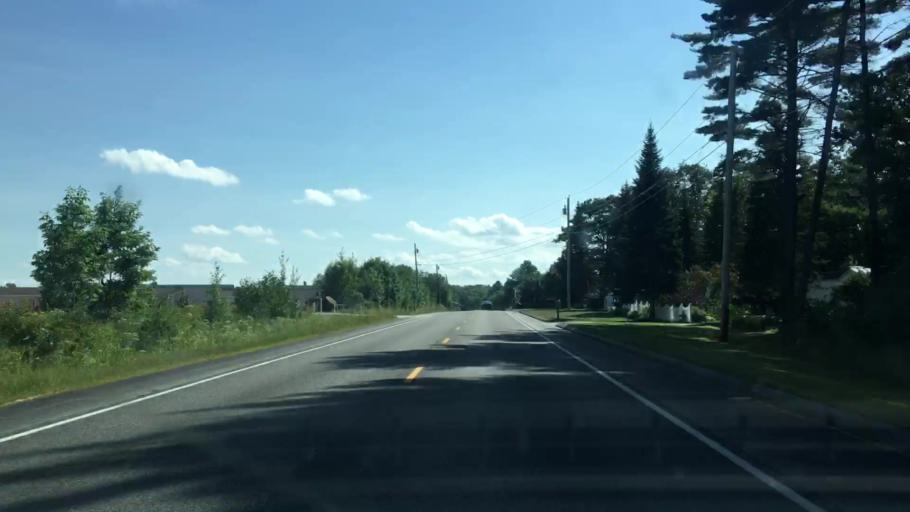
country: US
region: Maine
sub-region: Androscoggin County
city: Lisbon
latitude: 44.0622
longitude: -70.0852
